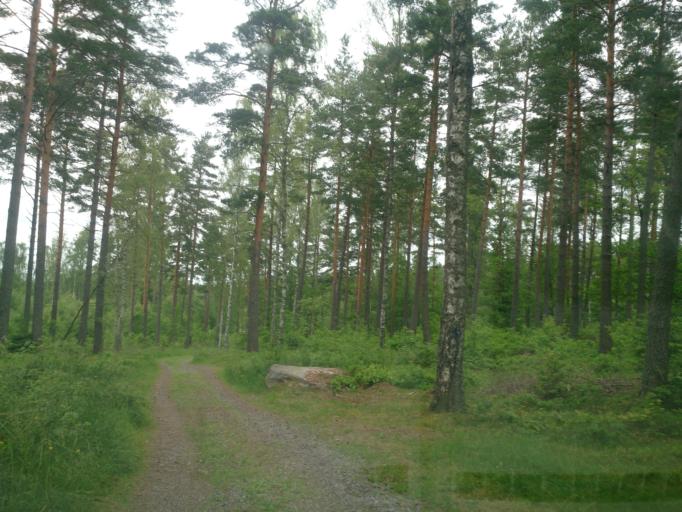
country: SE
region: OEstergoetland
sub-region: Atvidabergs Kommun
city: Atvidaberg
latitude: 58.2085
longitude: 16.0002
